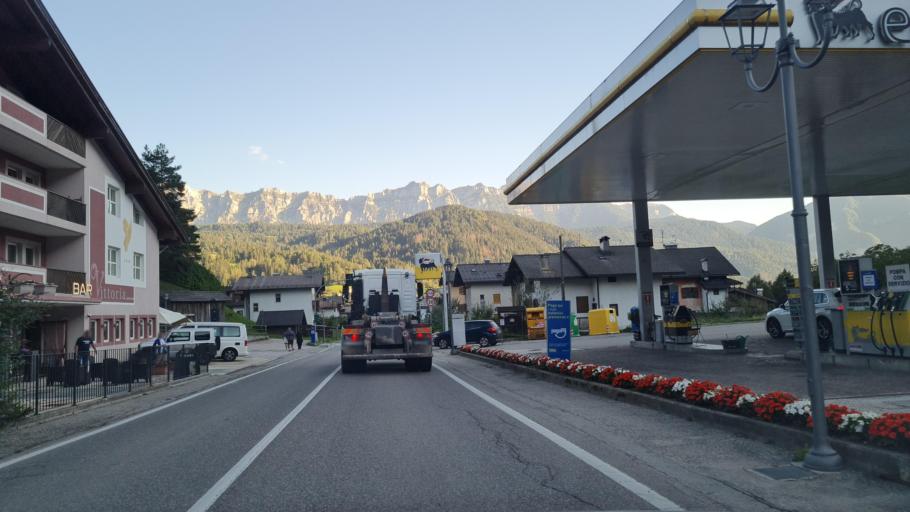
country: IT
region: Trentino-Alto Adige
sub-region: Provincia di Trento
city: Siror
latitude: 46.1822
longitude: 11.8317
